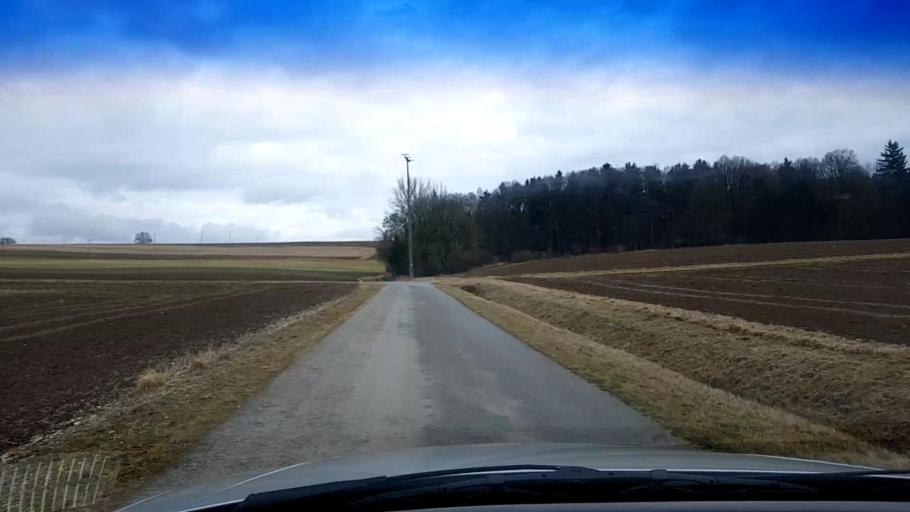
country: DE
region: Bavaria
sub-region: Upper Franconia
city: Zapfendorf
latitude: 50.0064
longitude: 10.9805
